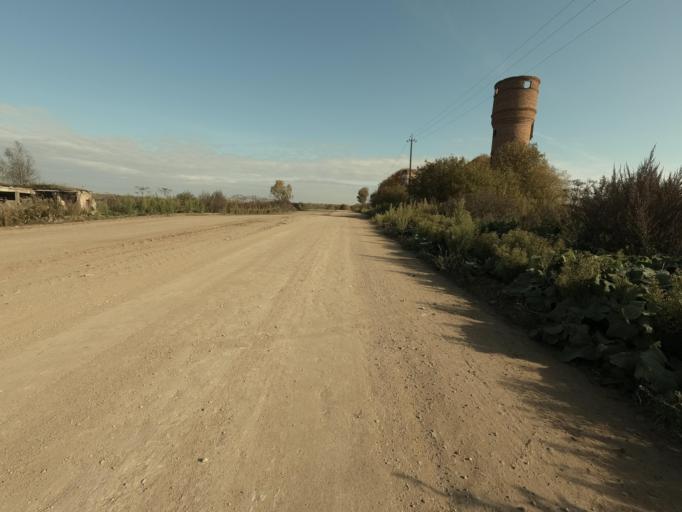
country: RU
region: Novgorod
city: Batetskiy
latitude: 58.8104
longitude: 30.6918
